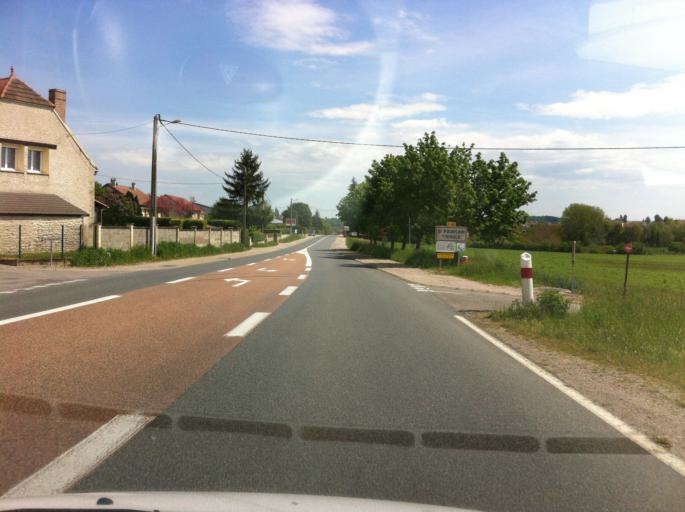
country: FR
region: Auvergne
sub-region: Departement de l'Allier
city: Saint-Pourcain-sur-Sioule
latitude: 46.3127
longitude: 3.2737
